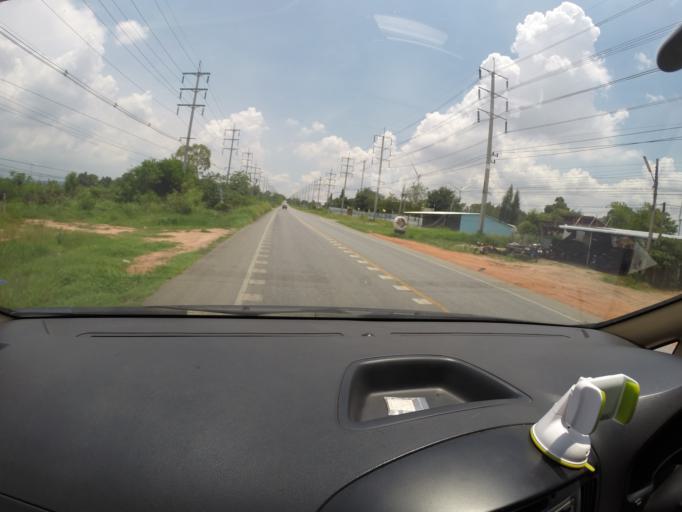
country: TH
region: Nakhon Ratchasima
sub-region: Amphoe Thepharak
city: Thepharak
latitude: 15.1193
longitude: 101.4922
